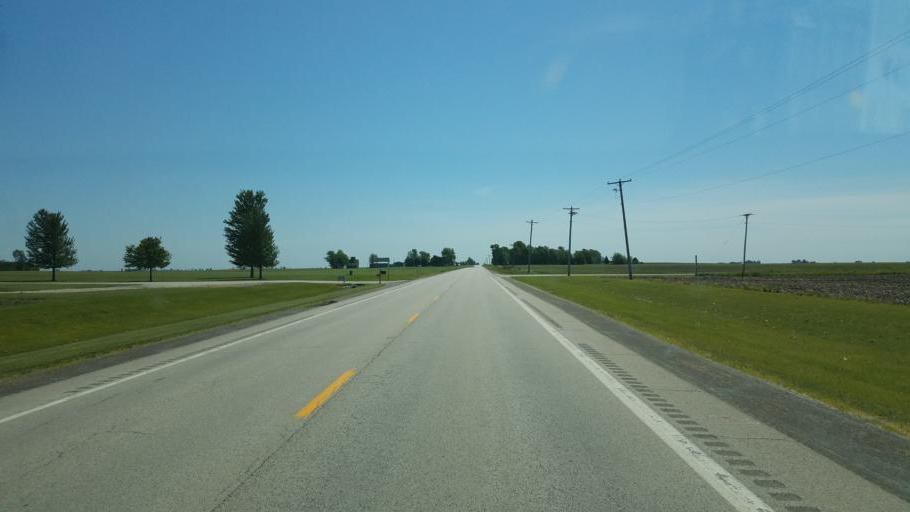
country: US
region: Illinois
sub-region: McLean County
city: Heyworth
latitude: 40.3123
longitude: -88.9217
